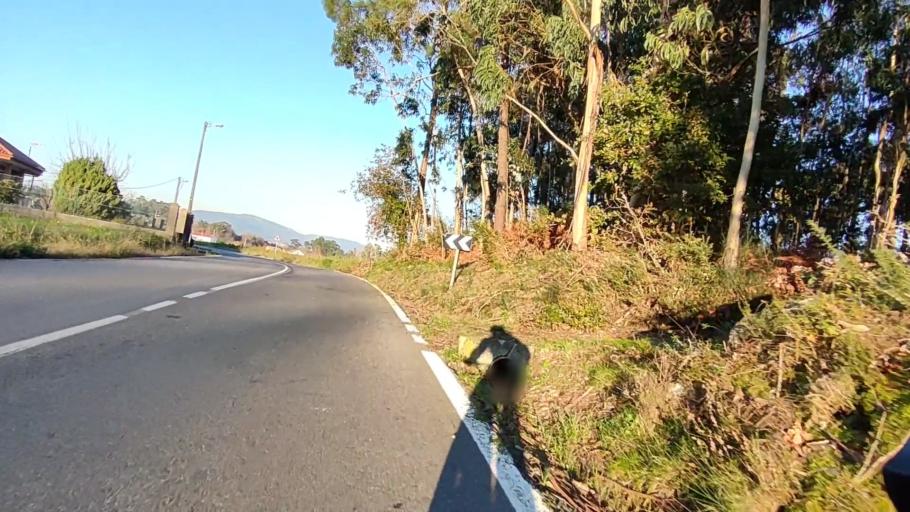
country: ES
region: Galicia
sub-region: Provincia da Coruna
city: Rianxo
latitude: 42.6334
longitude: -8.8583
